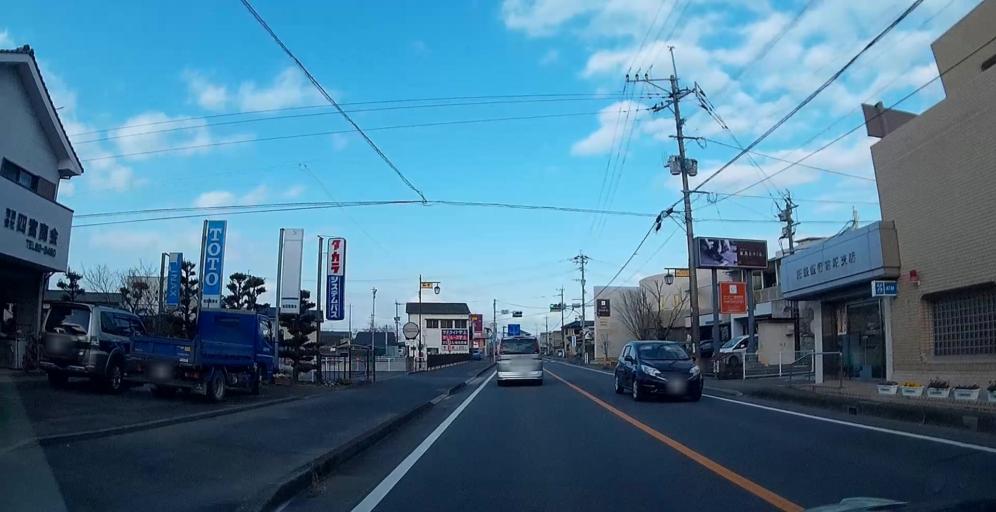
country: JP
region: Kumamoto
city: Yatsushiro
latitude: 32.5550
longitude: 130.6805
